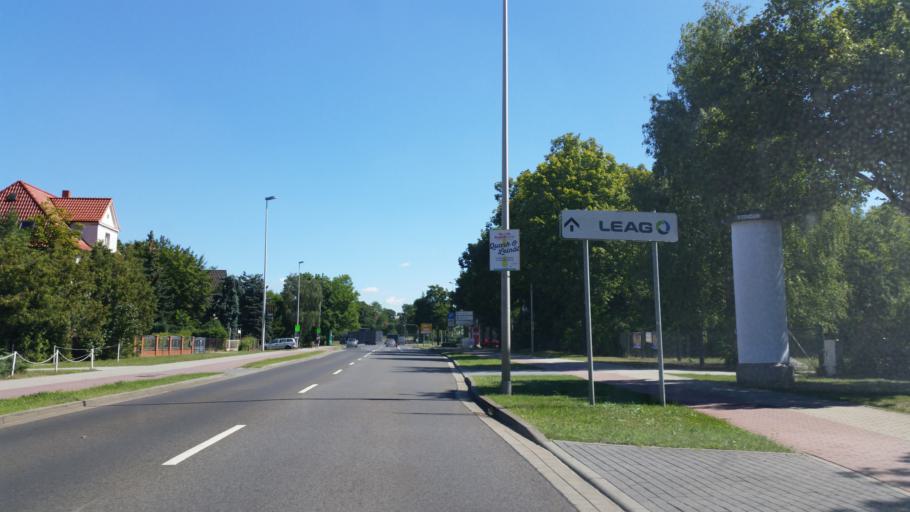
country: DE
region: Brandenburg
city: Cottbus
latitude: 51.7358
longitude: 14.3215
